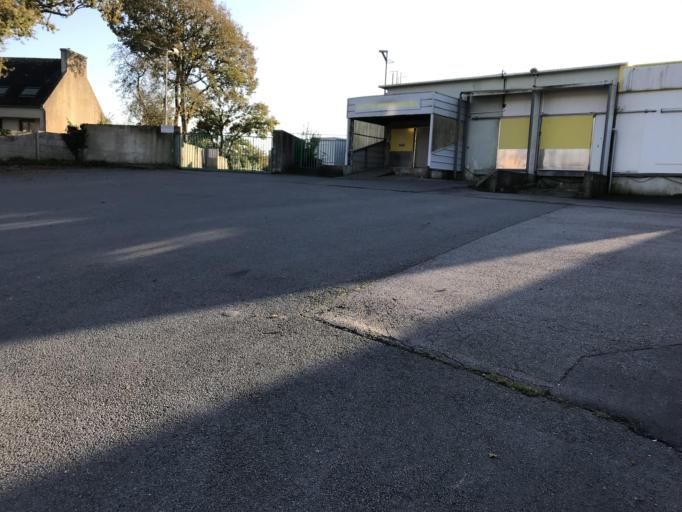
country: FR
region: Brittany
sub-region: Departement du Finistere
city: Le Faou
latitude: 48.2977
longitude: -4.1903
